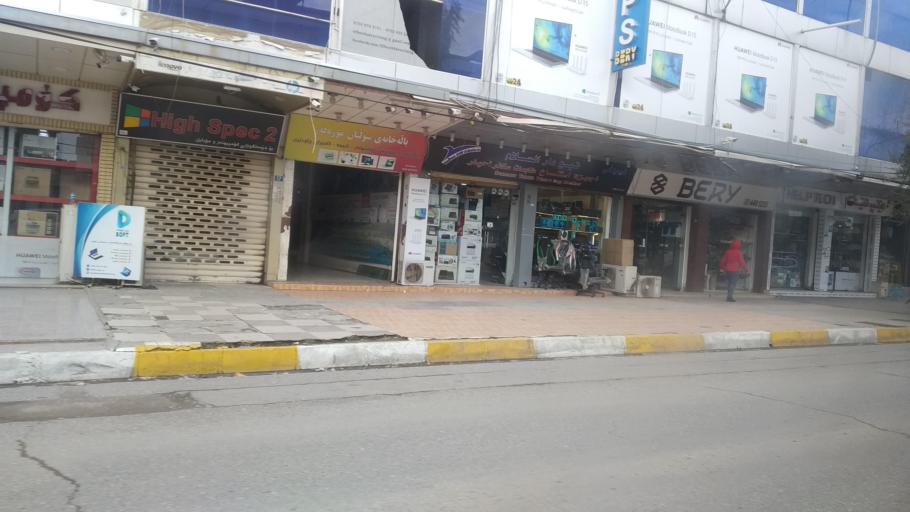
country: IQ
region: Arbil
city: Erbil
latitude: 36.1897
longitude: 44.0035
